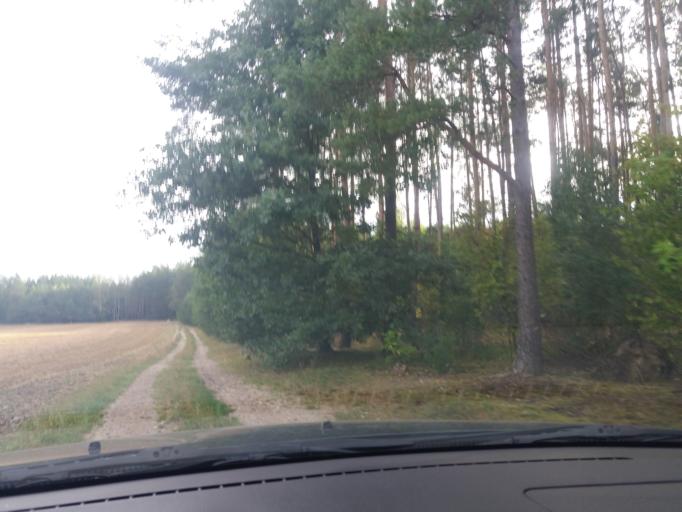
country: PL
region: Masovian Voivodeship
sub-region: Powiat mlawski
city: Wieczfnia Koscielna
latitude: 53.2179
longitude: 20.4572
